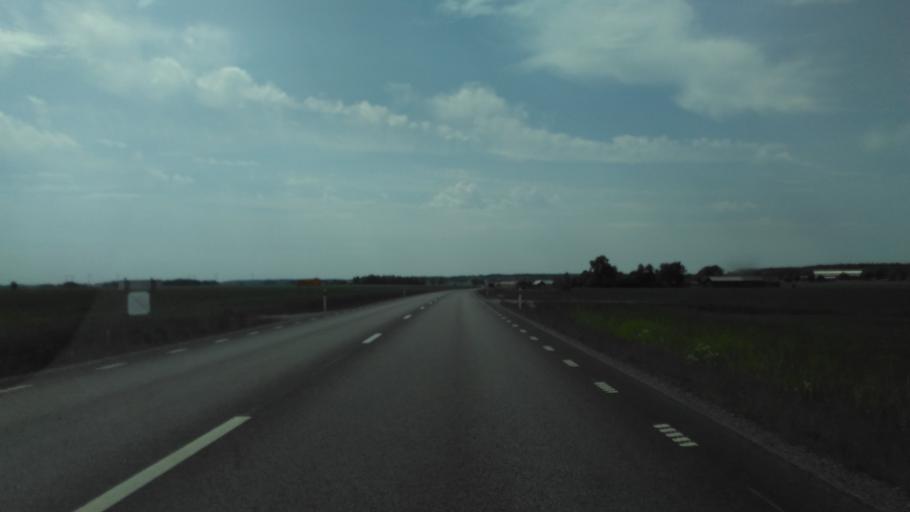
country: SE
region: Vaestra Goetaland
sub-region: Lidkopings Kommun
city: Lidkoping
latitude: 58.4775
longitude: 13.0778
